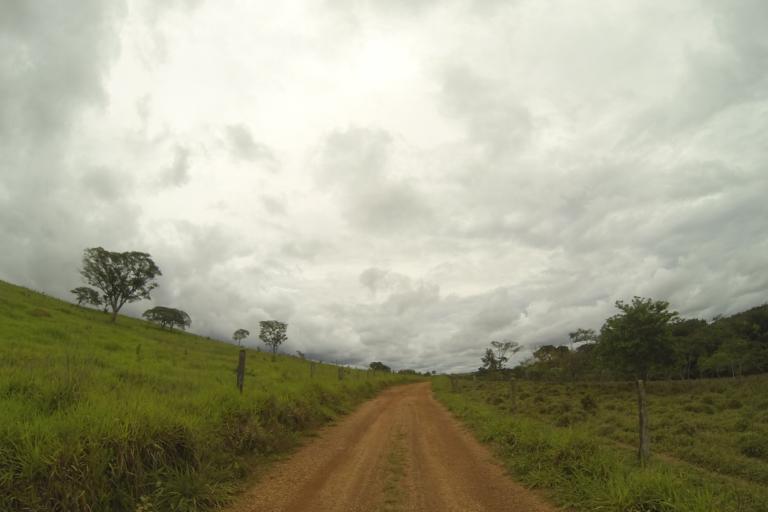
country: BR
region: Minas Gerais
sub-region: Ibia
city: Ibia
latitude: -19.7208
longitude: -46.5709
